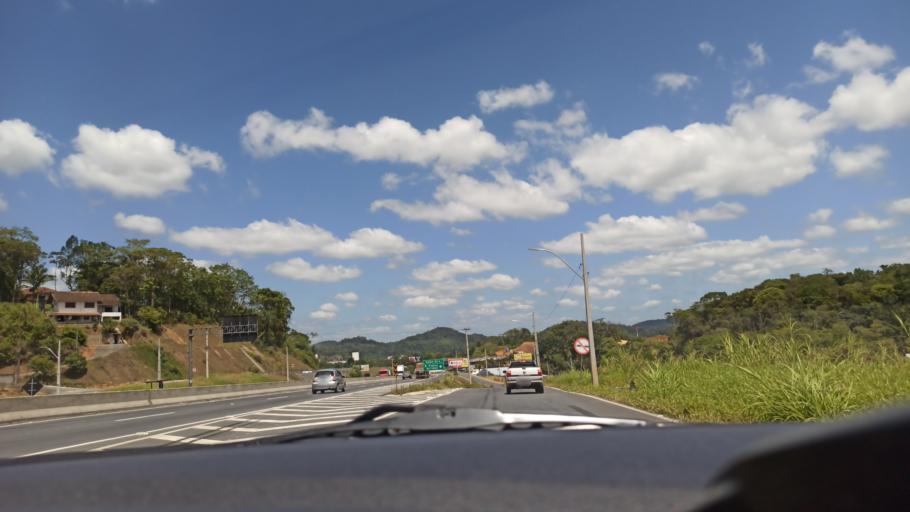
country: BR
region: Santa Catarina
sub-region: Blumenau
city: Blumenau
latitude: -26.8596
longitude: -49.0755
